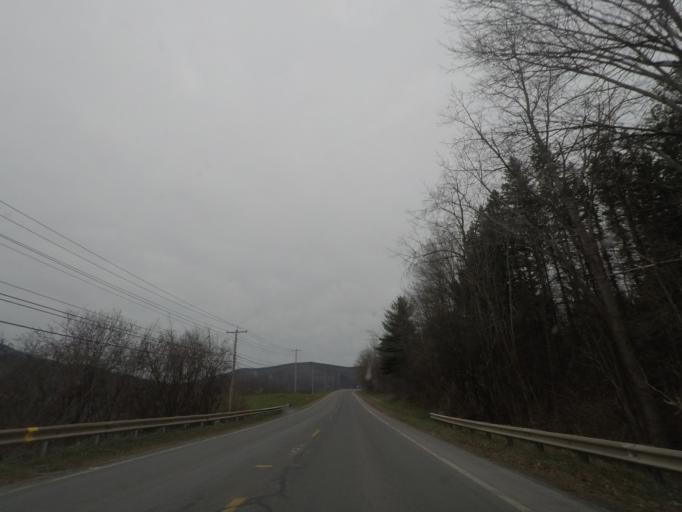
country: US
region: Massachusetts
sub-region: Berkshire County
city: Williamstown
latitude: 42.6691
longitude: -73.2382
